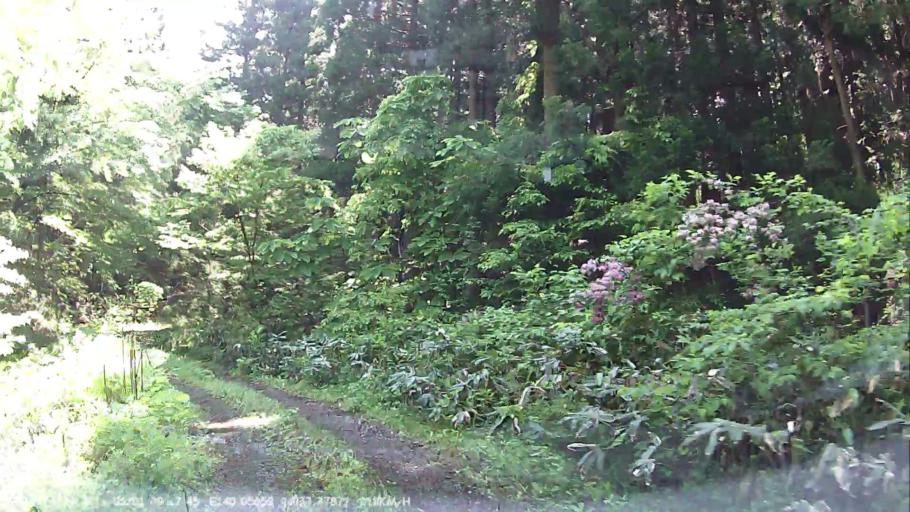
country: JP
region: Fukushima
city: Inawashiro
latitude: 37.3788
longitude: 140.0566
